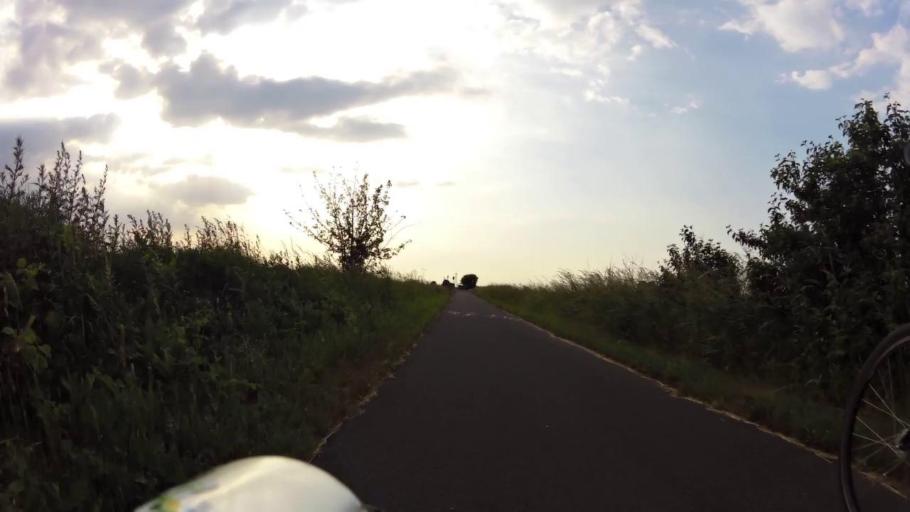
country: PL
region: Kujawsko-Pomorskie
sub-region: Powiat chelminski
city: Unislaw
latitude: 53.1764
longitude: 18.4131
